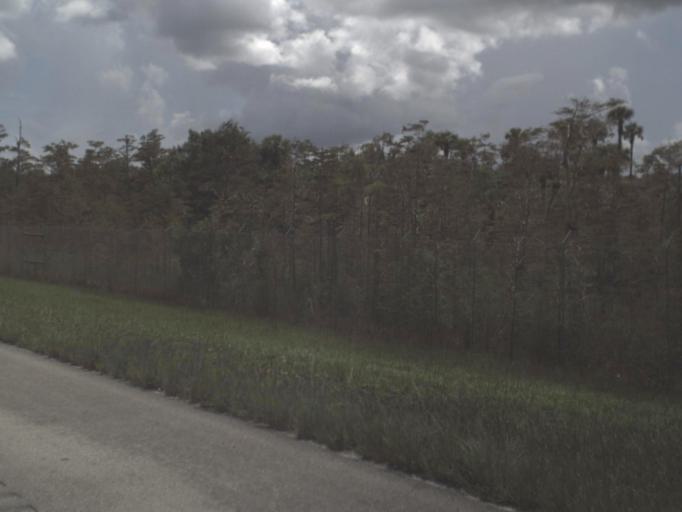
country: US
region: Florida
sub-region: Collier County
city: Immokalee
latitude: 26.1661
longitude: -81.2337
